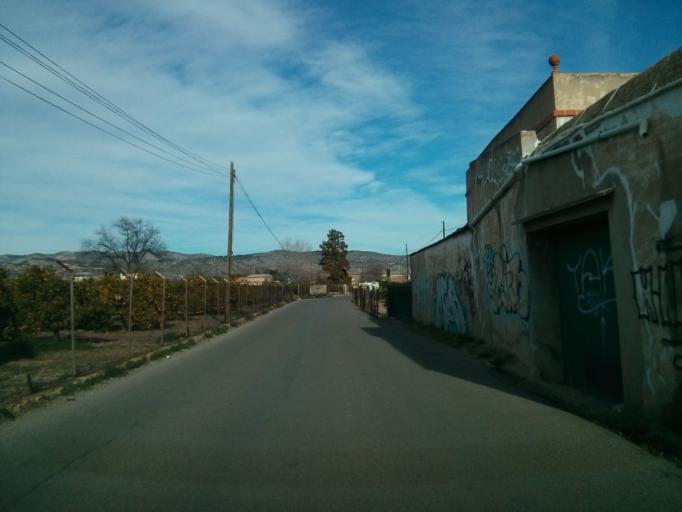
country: ES
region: Valencia
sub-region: Provincia de Castello
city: Castello de la Plana
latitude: 39.9940
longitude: -0.0206
